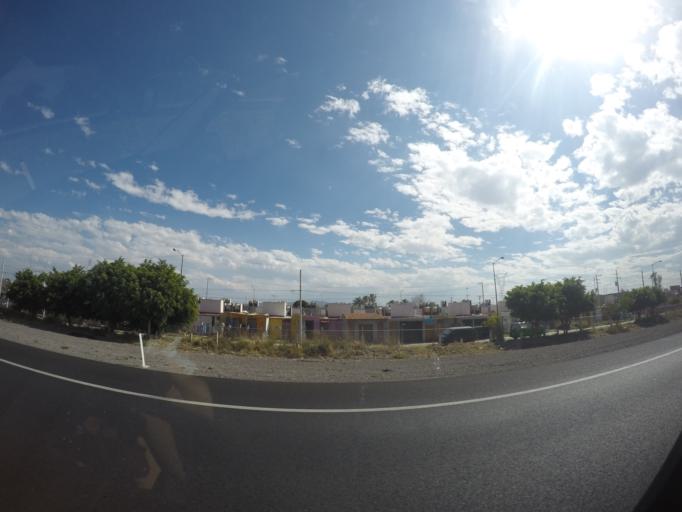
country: MX
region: Guanajuato
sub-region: Celaya
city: Roque
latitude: 20.5629
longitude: -100.8549
